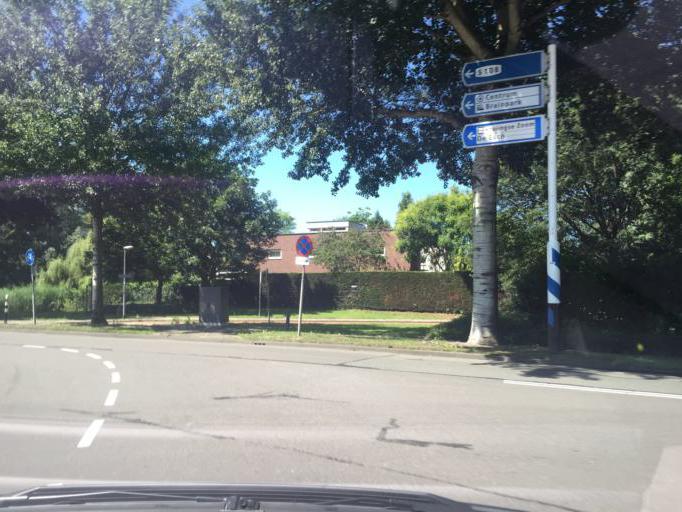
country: NL
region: South Holland
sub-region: Gemeente Rotterdam
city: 's-Gravenland
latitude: 51.9257
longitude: 4.5337
